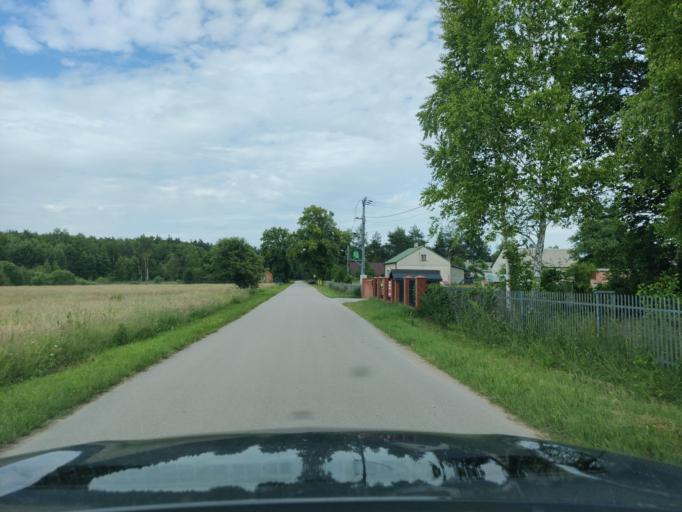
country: PL
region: Masovian Voivodeship
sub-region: Powiat pultuski
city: Obryte
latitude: 52.7365
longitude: 21.1713
